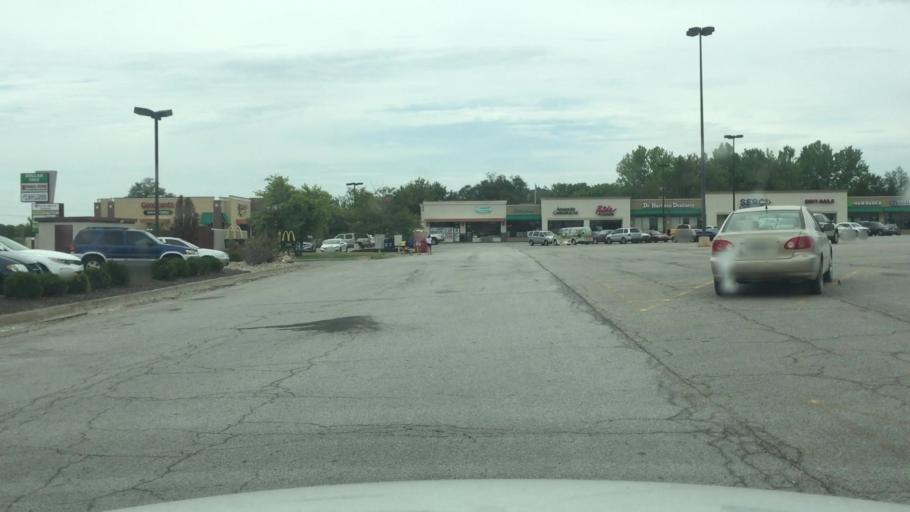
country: US
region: Kansas
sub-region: Wyandotte County
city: Bonner Springs
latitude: 39.0868
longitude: -94.8830
